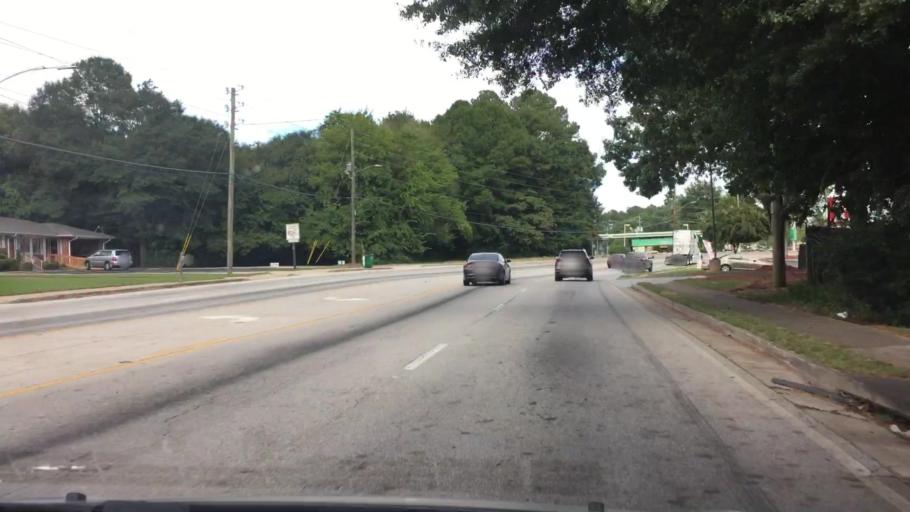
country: US
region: Georgia
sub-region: DeKalb County
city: Gresham Park
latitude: 33.6888
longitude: -84.3130
